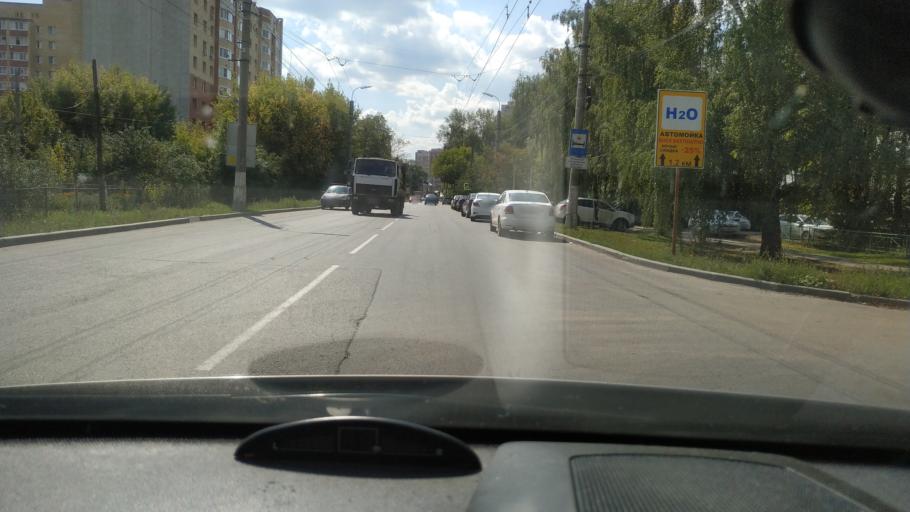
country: RU
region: Rjazan
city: Ryazan'
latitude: 54.6358
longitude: 39.6760
